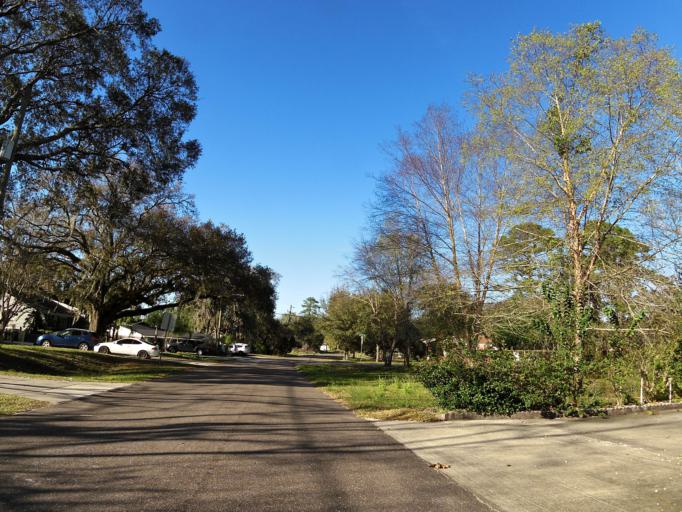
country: US
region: Florida
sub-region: Duval County
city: Jacksonville
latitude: 30.3984
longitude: -81.6772
